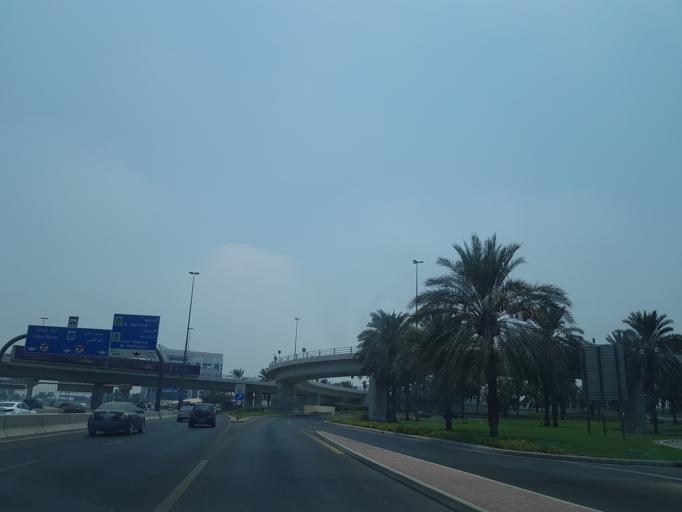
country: AE
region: Ash Shariqah
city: Sharjah
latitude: 25.2511
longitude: 55.3361
